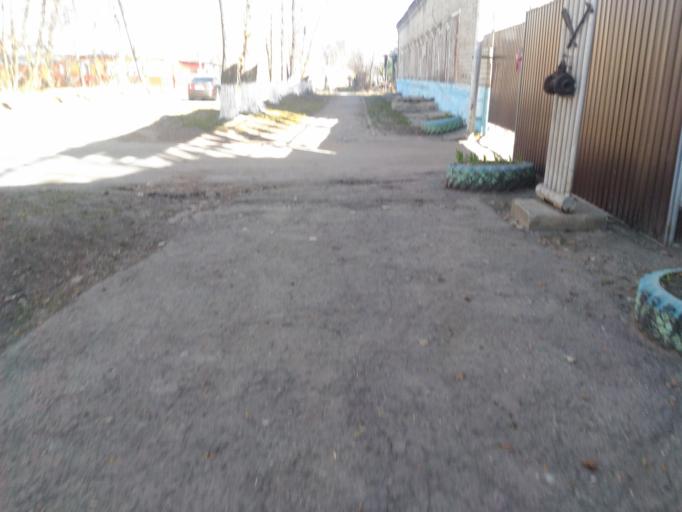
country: RU
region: Ulyanovsk
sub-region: Ulyanovskiy Rayon
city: Ulyanovsk
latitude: 54.3462
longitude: 48.3813
